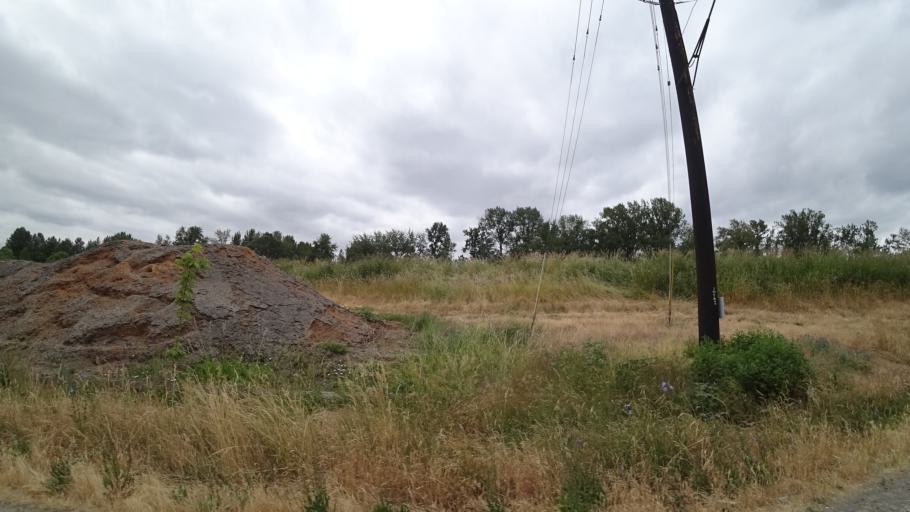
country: US
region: Washington
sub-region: Clark County
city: Vancouver
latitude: 45.5895
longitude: -122.6840
